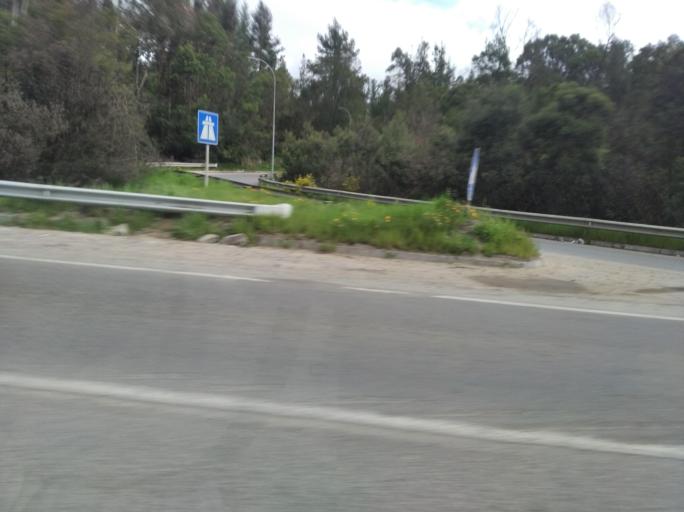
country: CL
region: Valparaiso
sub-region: Provincia de Valparaiso
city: Vina del Mar
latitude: -33.1093
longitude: -71.5548
